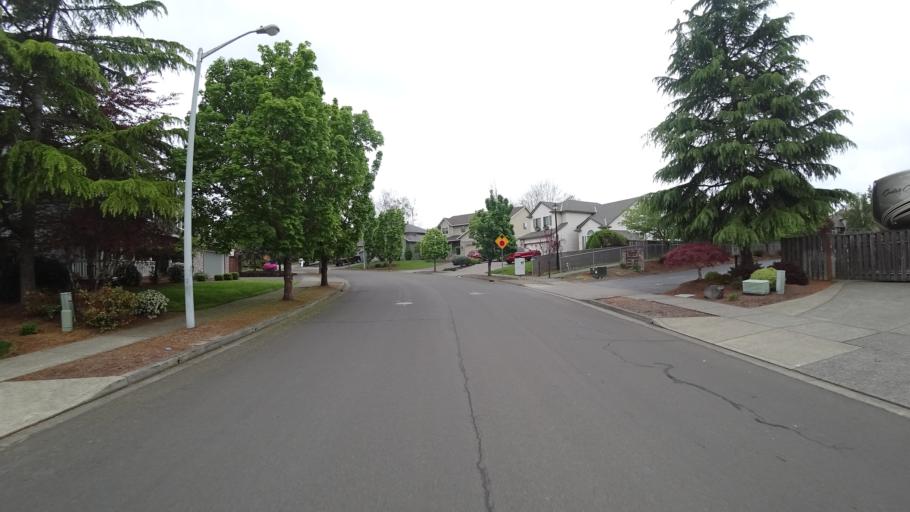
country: US
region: Oregon
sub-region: Washington County
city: Hillsboro
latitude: 45.5463
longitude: -122.9831
